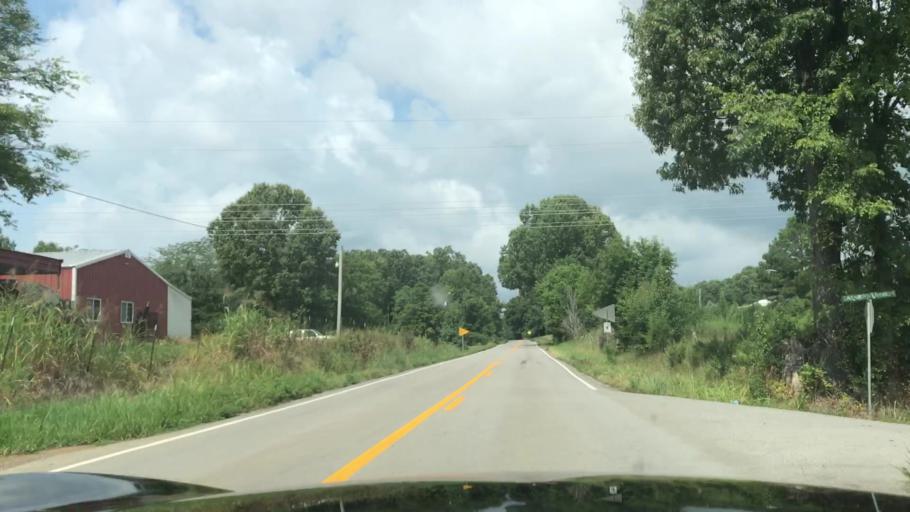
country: US
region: Kentucky
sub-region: Ohio County
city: Beaver Dam
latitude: 37.2126
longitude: -86.9193
